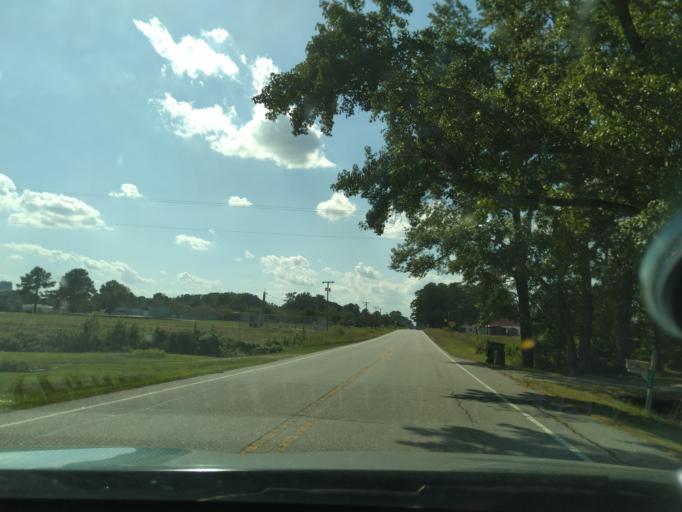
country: US
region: North Carolina
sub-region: Martin County
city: Robersonville
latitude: 35.8286
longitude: -77.2329
